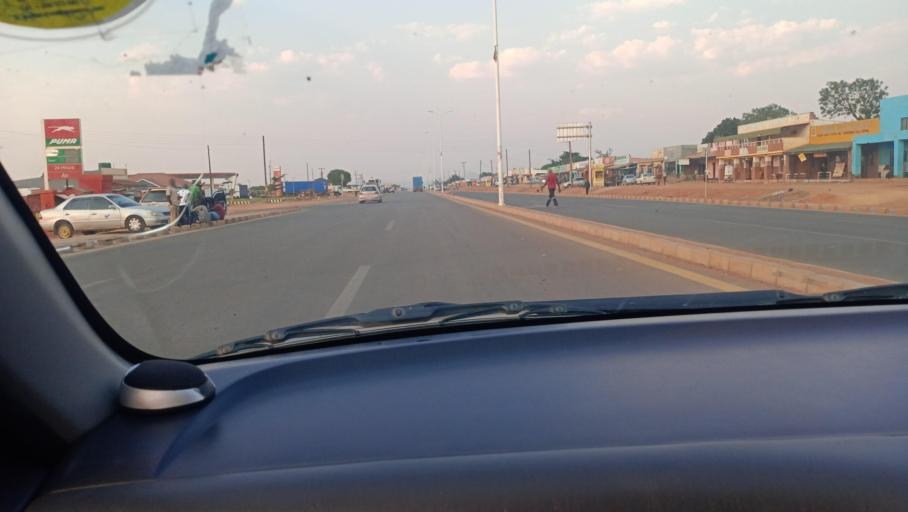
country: ZM
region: Northern
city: Mpika
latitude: -11.8438
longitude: 31.4438
